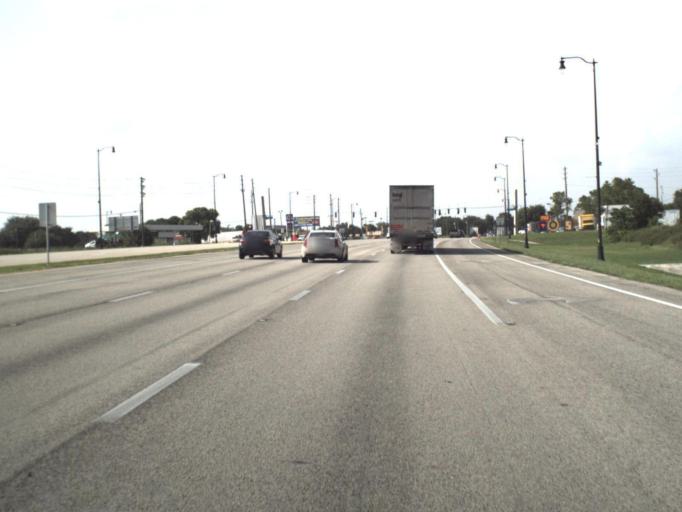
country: US
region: Florida
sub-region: Polk County
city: Lake Hamilton
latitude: 28.0786
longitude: -81.6488
